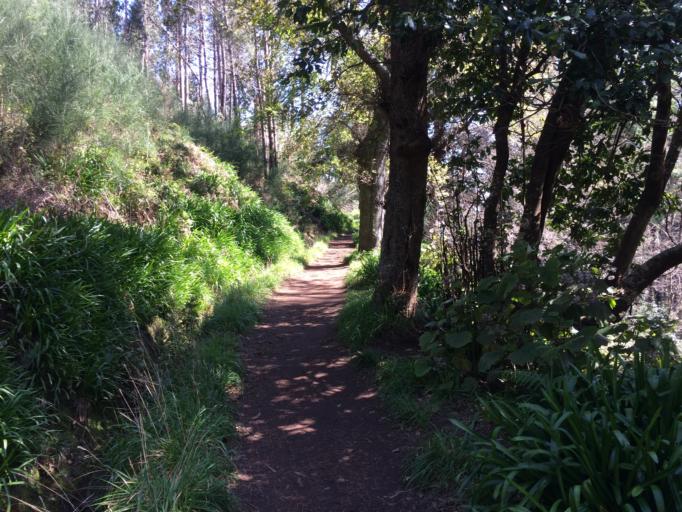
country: PT
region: Madeira
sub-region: Santa Cruz
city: Camacha
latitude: 32.6791
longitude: -16.8609
